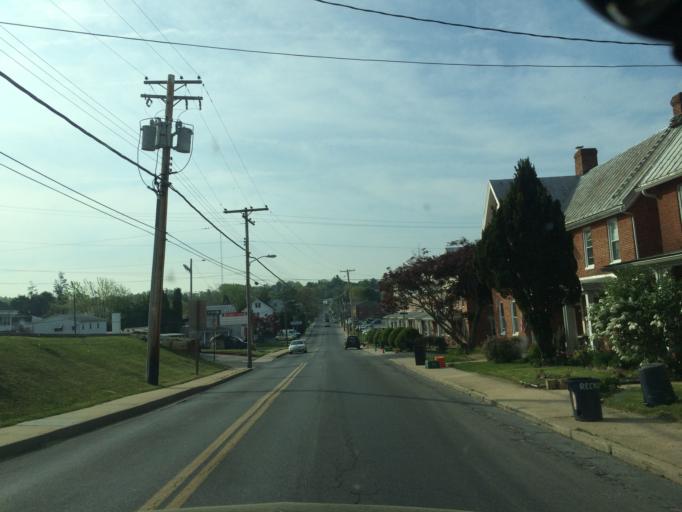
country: US
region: Maryland
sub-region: Carroll County
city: Westminster
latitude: 39.5697
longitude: -76.9924
